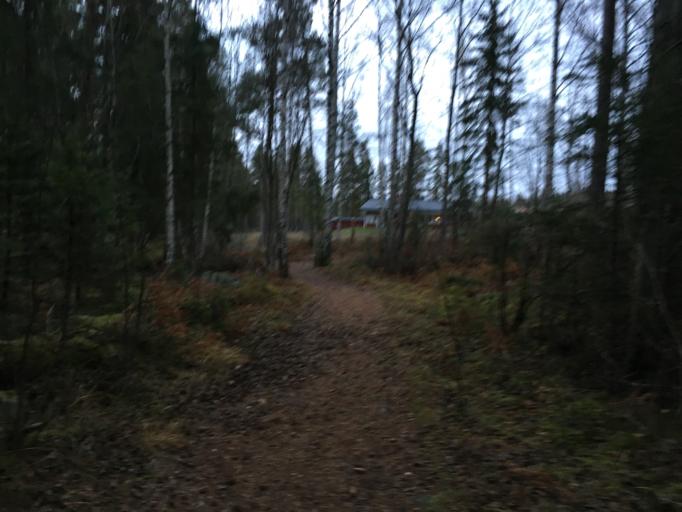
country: SE
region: Uppsala
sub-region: Alvkarleby Kommun
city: AElvkarleby
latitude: 60.6494
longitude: 17.5571
